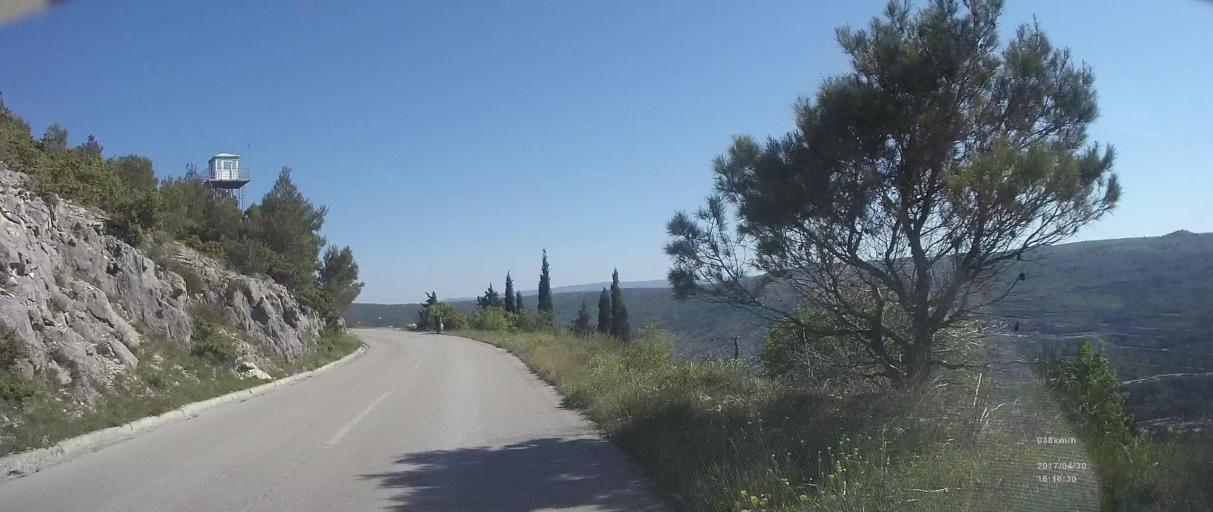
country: HR
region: Splitsko-Dalmatinska
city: Srinjine
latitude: 43.5026
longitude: 16.6056
